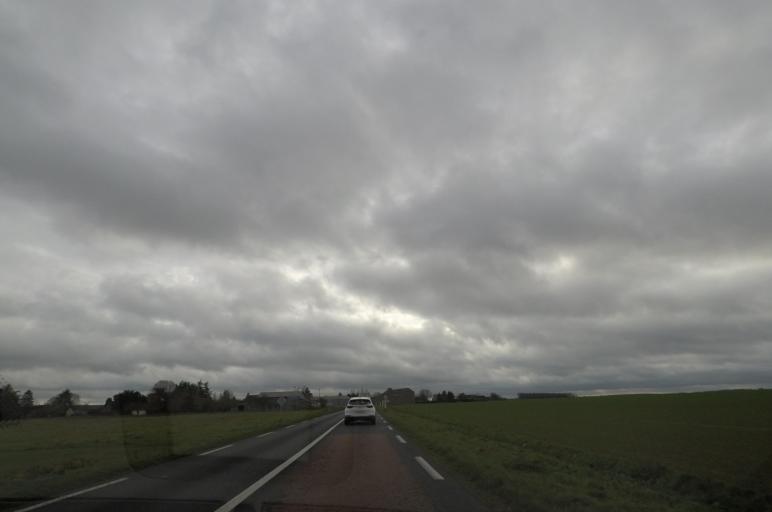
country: FR
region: Centre
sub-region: Departement du Loir-et-Cher
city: Herbault
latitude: 47.6904
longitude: 1.1910
